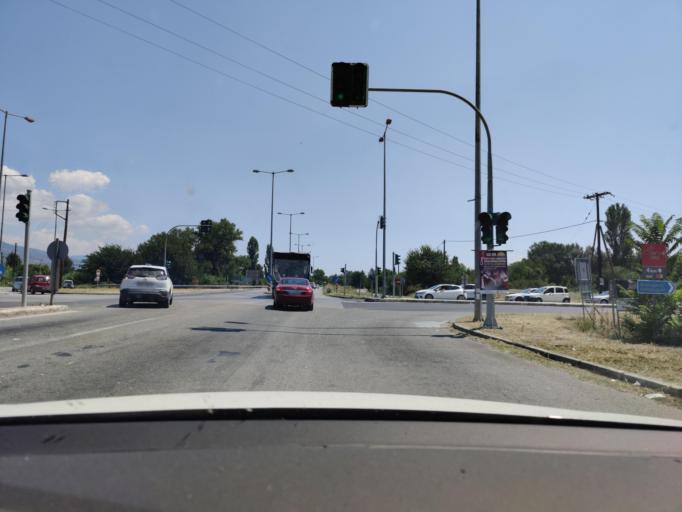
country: GR
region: Central Macedonia
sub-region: Nomos Serron
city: Serres
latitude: 41.0757
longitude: 23.5398
